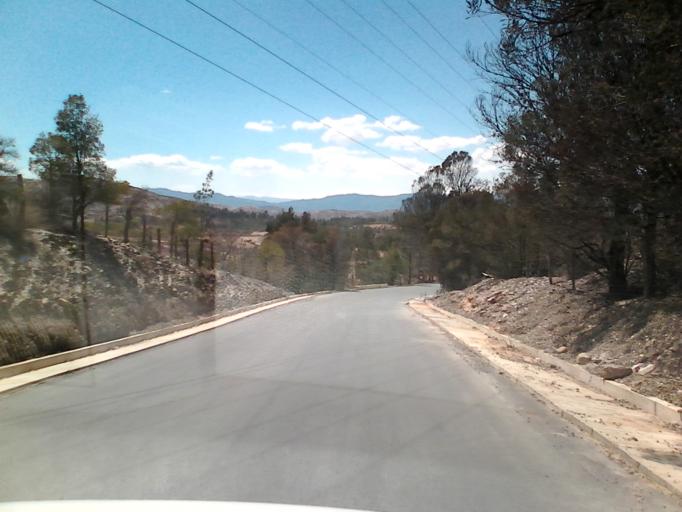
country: CO
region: Boyaca
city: Villa de Leiva
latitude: 5.6239
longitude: -73.5743
